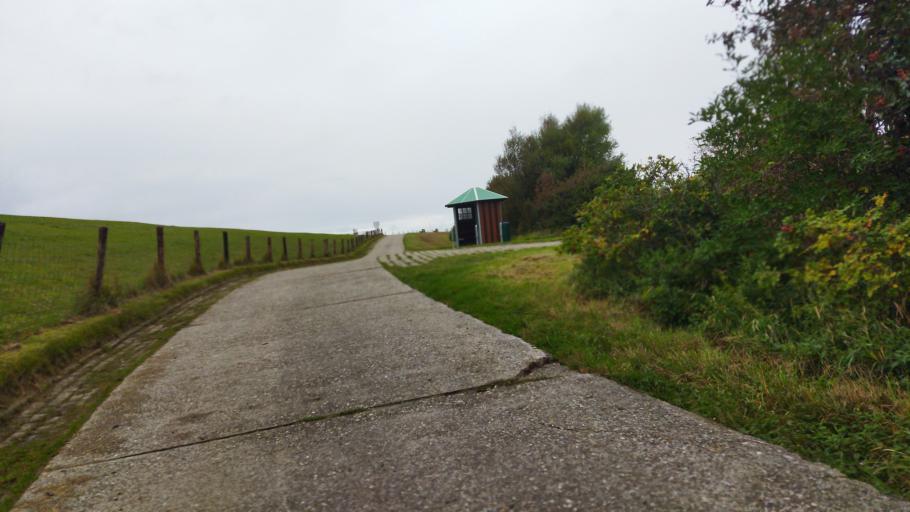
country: DE
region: Lower Saxony
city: Hinte
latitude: 53.4832
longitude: 7.0290
